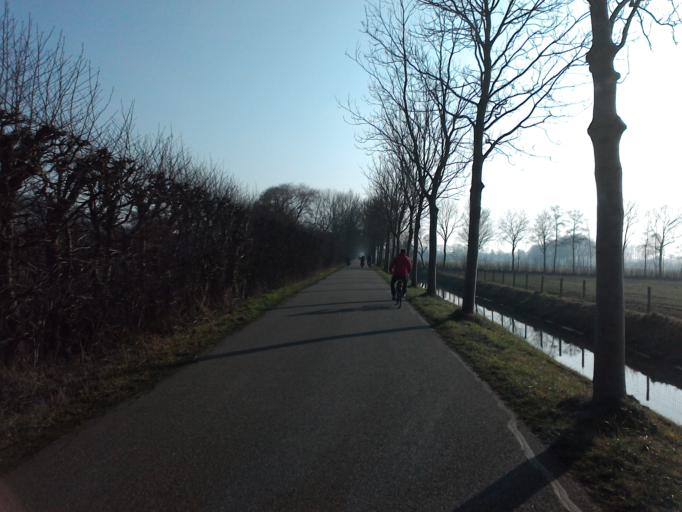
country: NL
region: Utrecht
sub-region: Gemeente Bunnik
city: Bunnik
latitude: 52.0840
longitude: 5.1934
